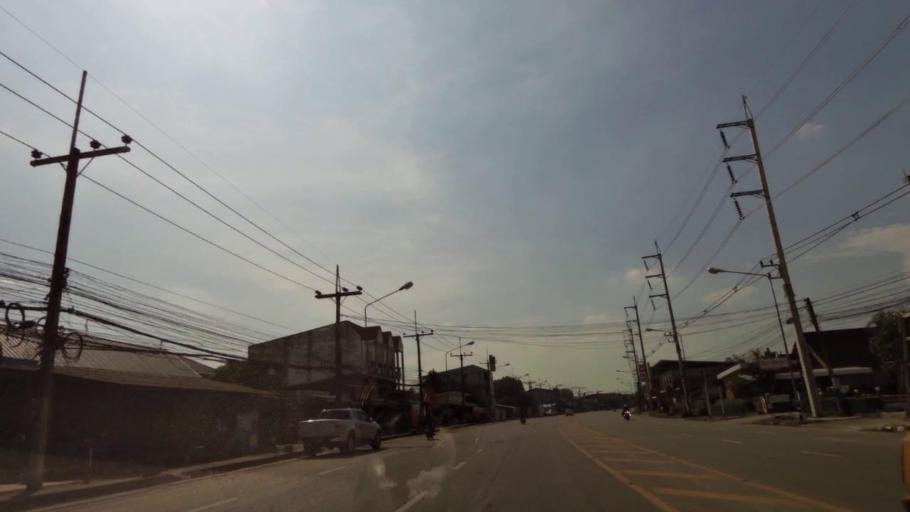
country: TH
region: Chiang Rai
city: Chiang Rai
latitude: 19.8836
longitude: 99.7993
